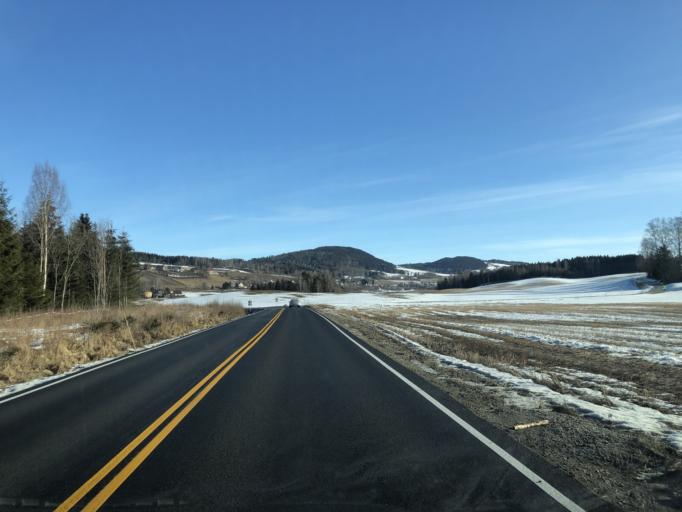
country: NO
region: Hedmark
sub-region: Ringsaker
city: Moelv
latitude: 60.9051
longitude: 10.7344
